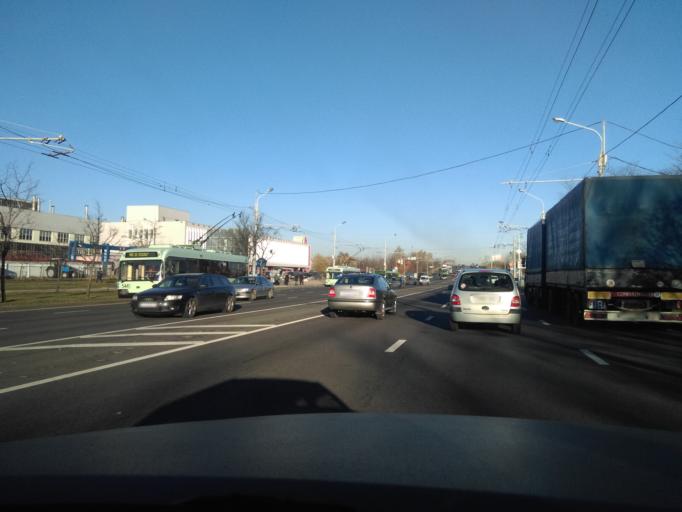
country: BY
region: Minsk
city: Minsk
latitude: 53.8986
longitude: 27.6405
